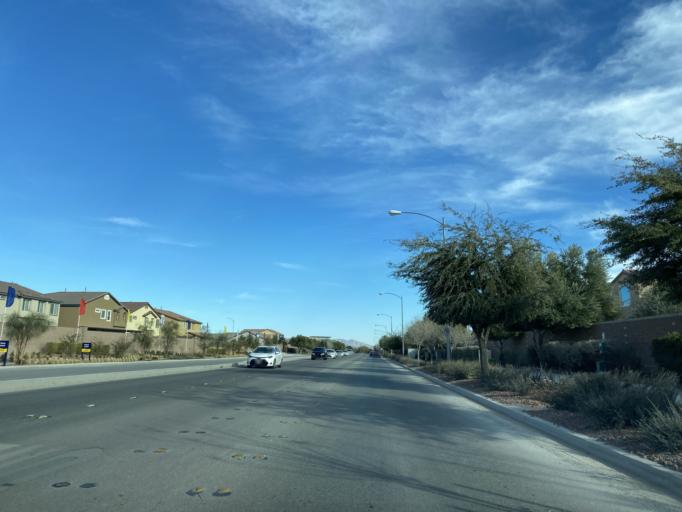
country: US
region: Nevada
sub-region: Clark County
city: North Las Vegas
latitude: 36.2911
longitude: -115.1958
